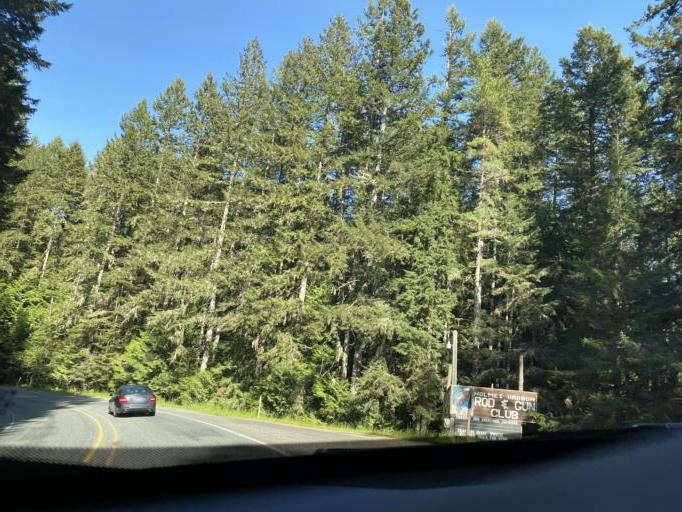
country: US
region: Washington
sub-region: Island County
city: Langley
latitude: 48.0312
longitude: -122.4335
